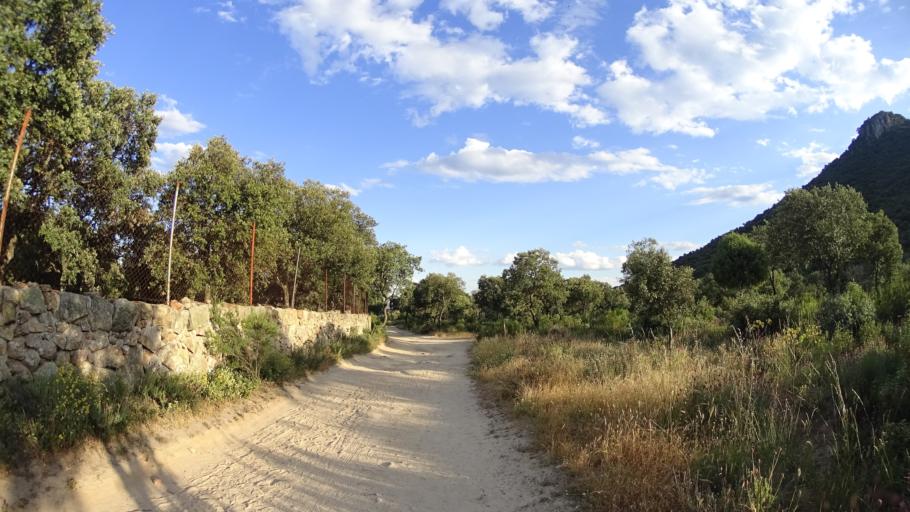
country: ES
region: Madrid
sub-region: Provincia de Madrid
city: Hoyo de Manzanares
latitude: 40.6279
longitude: -3.9167
